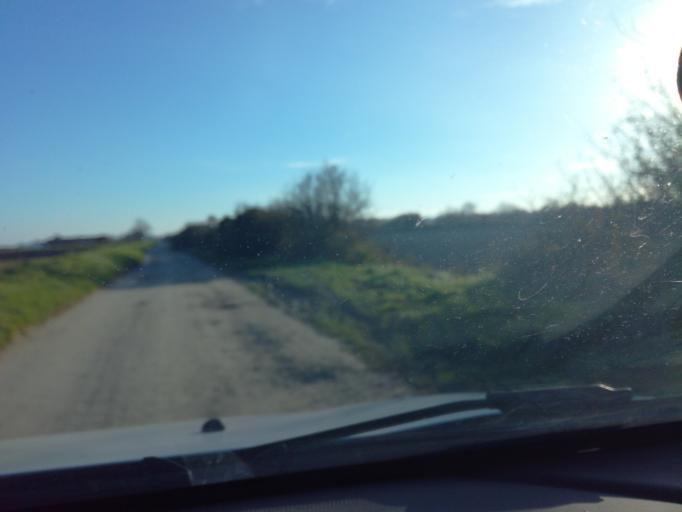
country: FR
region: Brittany
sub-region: Departement d'Ille-et-Vilaine
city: Saint-Meloir-des-Ondes
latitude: 48.6411
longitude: -1.8694
